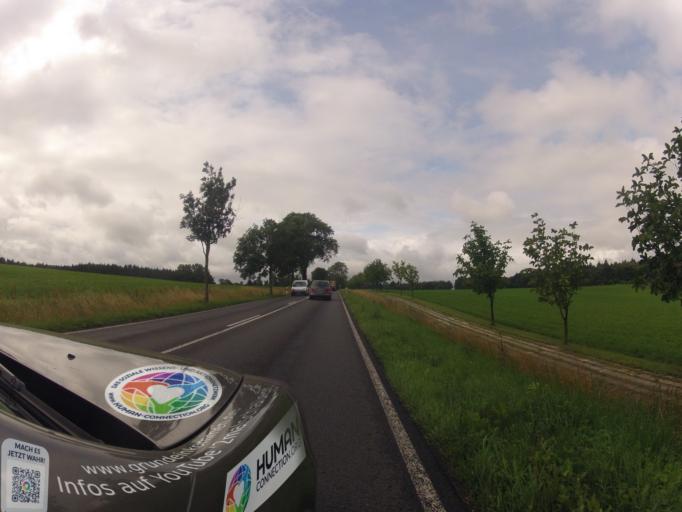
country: DE
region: Mecklenburg-Vorpommern
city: Anklam
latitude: 53.9050
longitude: 13.7416
